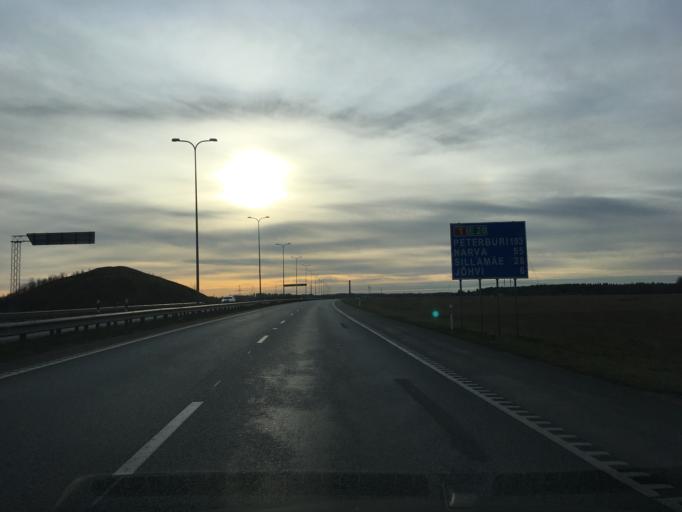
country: EE
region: Ida-Virumaa
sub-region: Kohtla-Jaerve linn
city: Kohtla-Jarve
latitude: 59.3977
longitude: 27.3330
